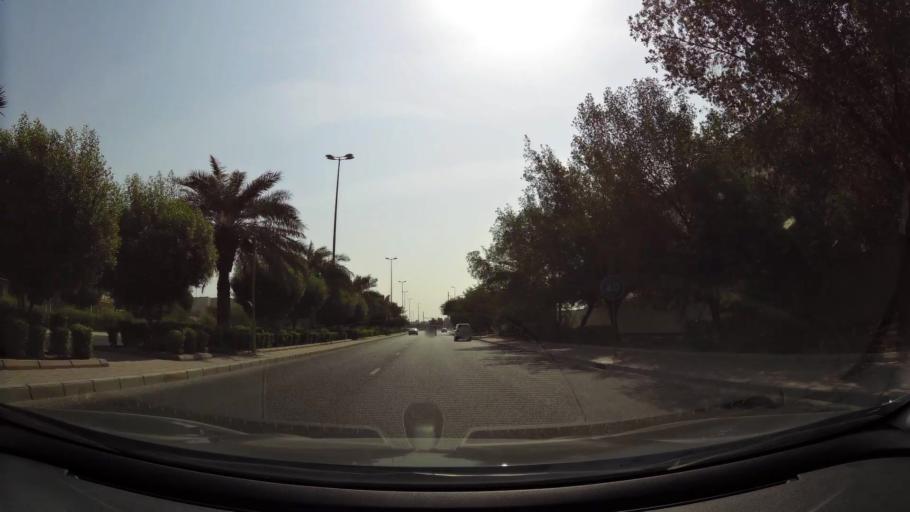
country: KW
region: Al Ahmadi
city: Al Mahbulah
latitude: 29.1232
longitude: 48.1333
